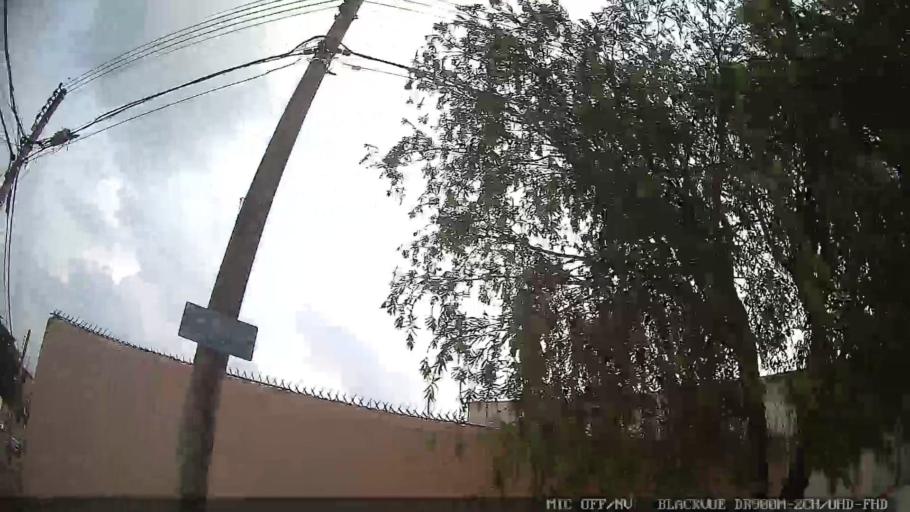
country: BR
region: Sao Paulo
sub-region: Braganca Paulista
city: Braganca Paulista
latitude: -22.9504
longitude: -46.5371
